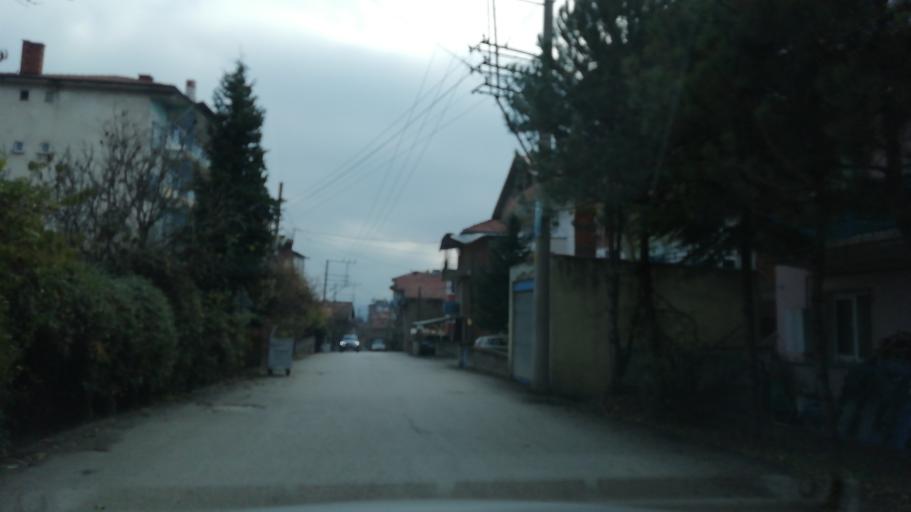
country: TR
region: Karabuk
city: Karabuk
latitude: 41.2223
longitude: 32.6265
